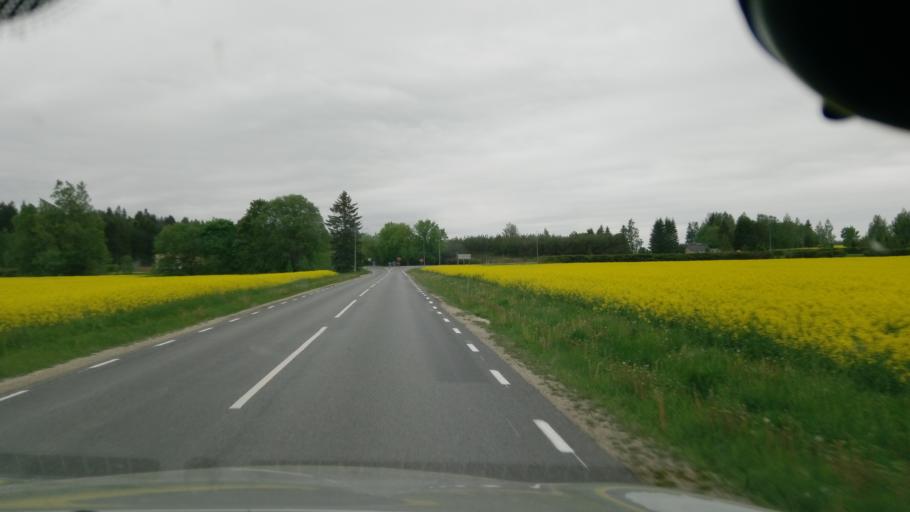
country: EE
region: Jaervamaa
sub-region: Koeru vald
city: Koeru
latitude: 58.9837
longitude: 26.0487
